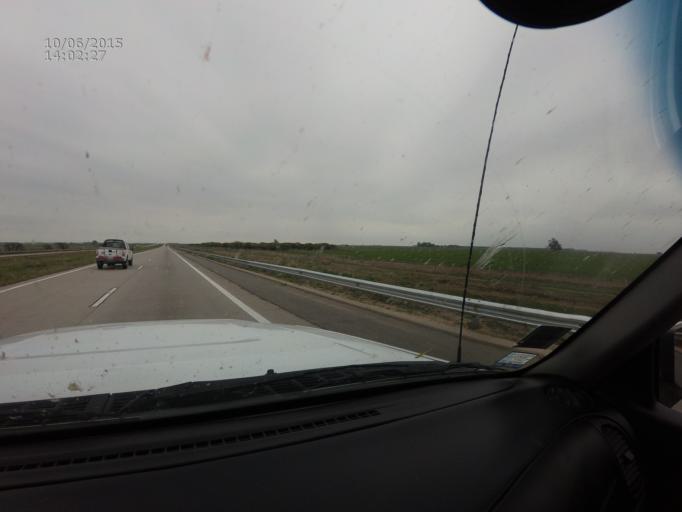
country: AR
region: Cordoba
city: Morrison
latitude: -32.5284
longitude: -62.9313
